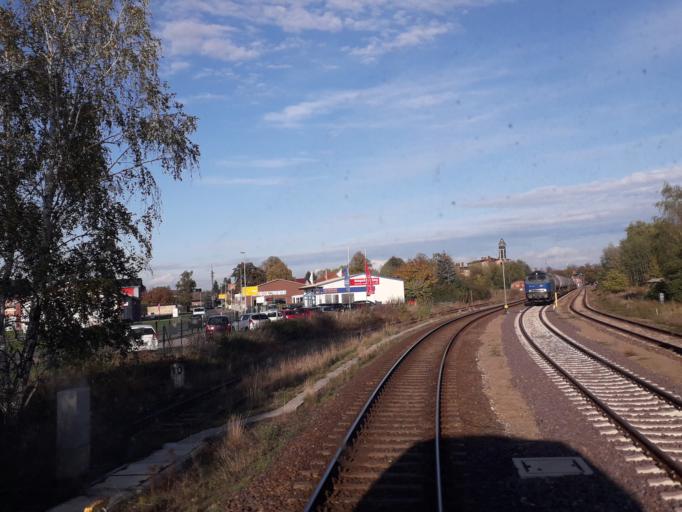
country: DE
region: Brandenburg
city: Perleberg
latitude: 53.0681
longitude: 11.8441
